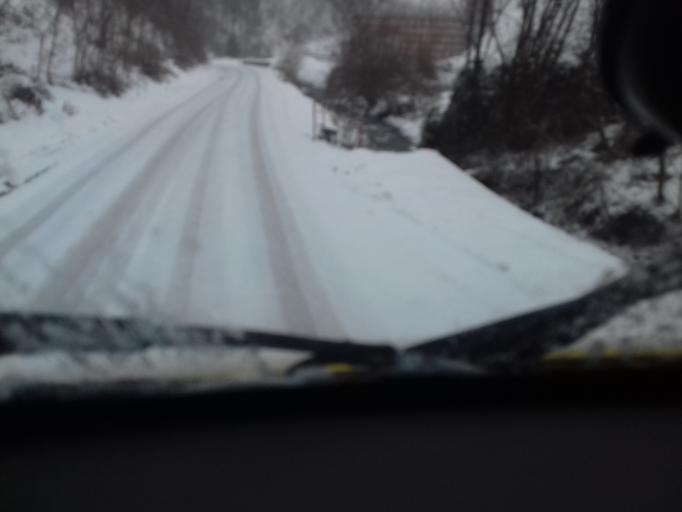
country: BA
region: Federation of Bosnia and Herzegovina
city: Zeljezno Polje
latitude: 44.3351
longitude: 17.8895
